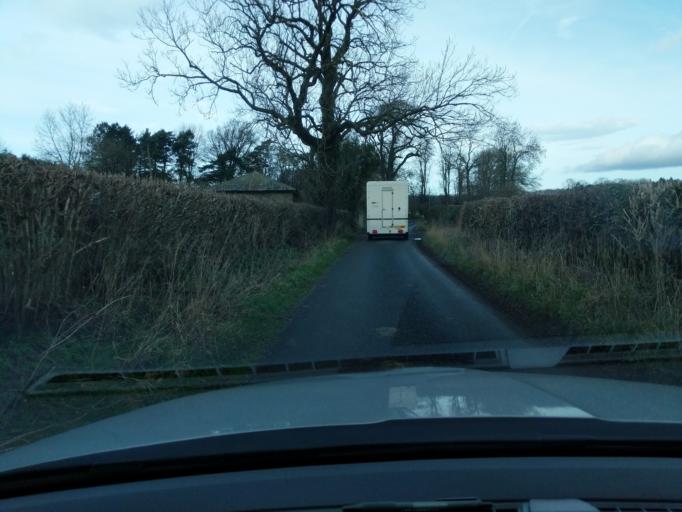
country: GB
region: England
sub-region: North Yorkshire
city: Catterick
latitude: 54.3678
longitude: -1.6687
